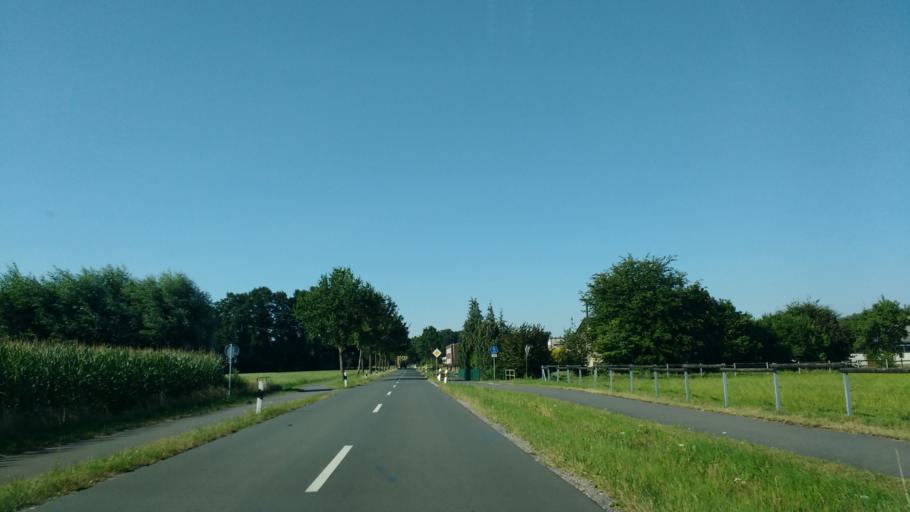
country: DE
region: North Rhine-Westphalia
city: Geseke
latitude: 51.7097
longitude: 8.4897
